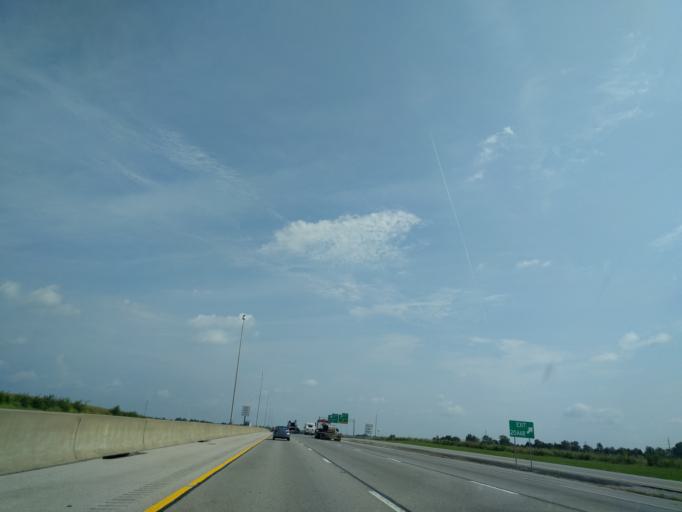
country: US
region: Kentucky
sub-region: Warren County
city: Plano
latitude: 36.9035
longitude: -86.4358
